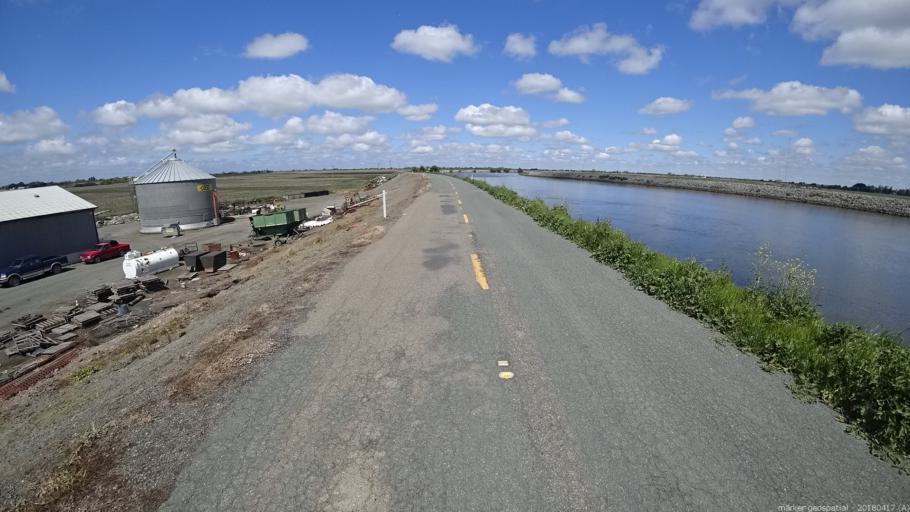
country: US
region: California
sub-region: Sacramento County
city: Walnut Grove
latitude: 38.1898
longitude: -121.5274
